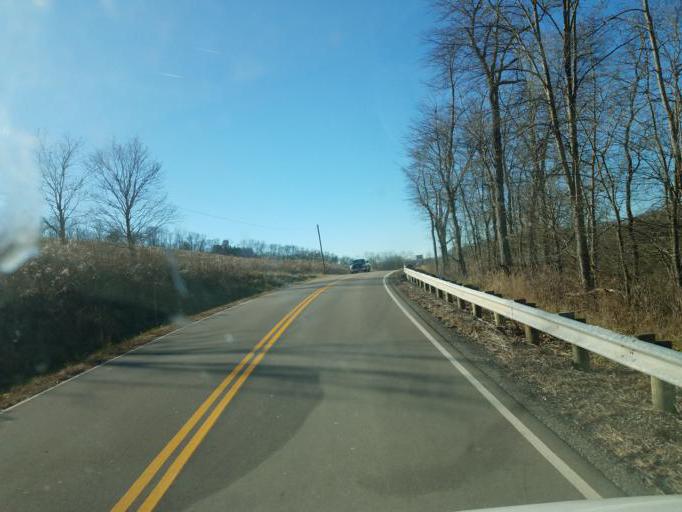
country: US
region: Ohio
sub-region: Muskingum County
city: Dresden
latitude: 40.2363
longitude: -82.0584
